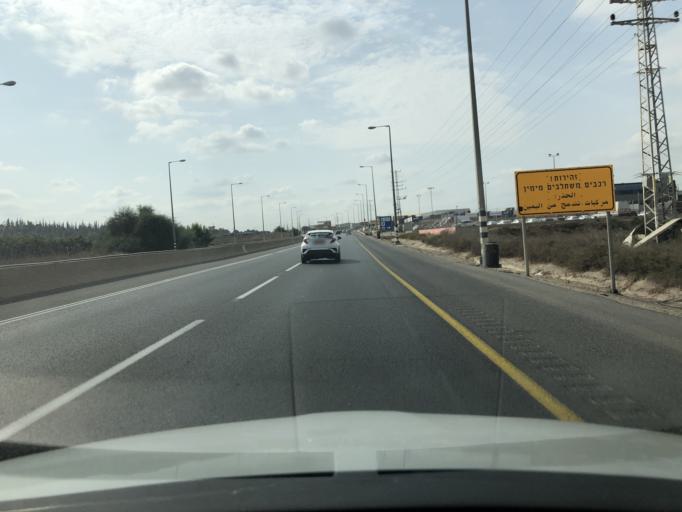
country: IL
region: Central District
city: Tirah
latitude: 32.2286
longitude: 34.9826
